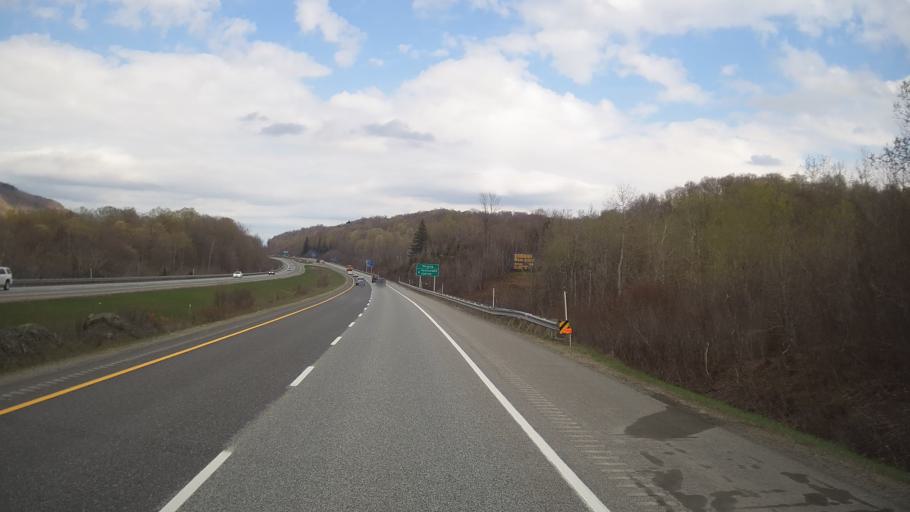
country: CA
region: Quebec
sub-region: Estrie
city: Magog
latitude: 45.2893
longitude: -72.2571
